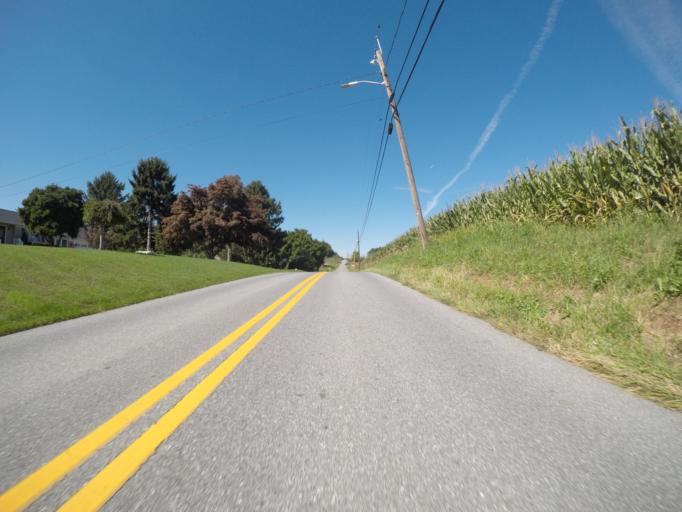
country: US
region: Maryland
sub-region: Baltimore County
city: Reisterstown
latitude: 39.5333
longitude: -76.7836
